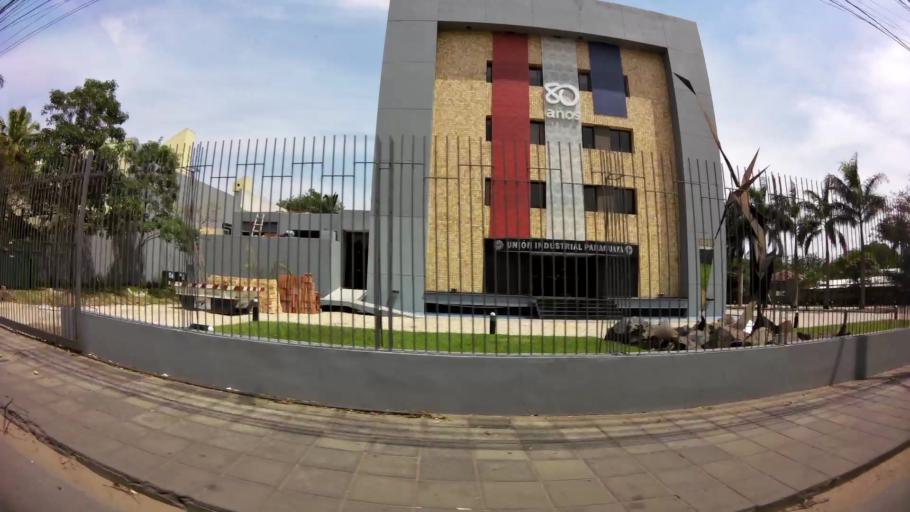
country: PY
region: Asuncion
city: Asuncion
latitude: -25.2833
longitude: -57.5878
